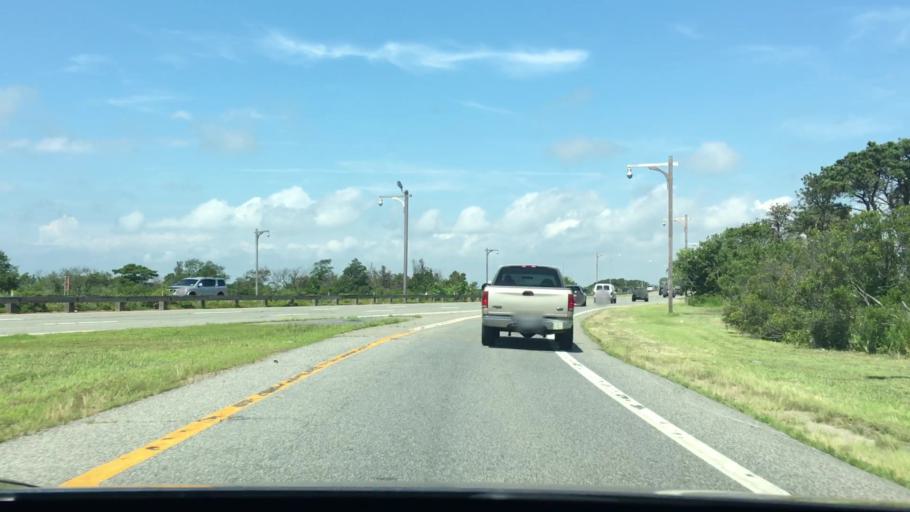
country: US
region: New York
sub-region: Nassau County
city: Point Lookout
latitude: 40.6136
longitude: -73.5514
